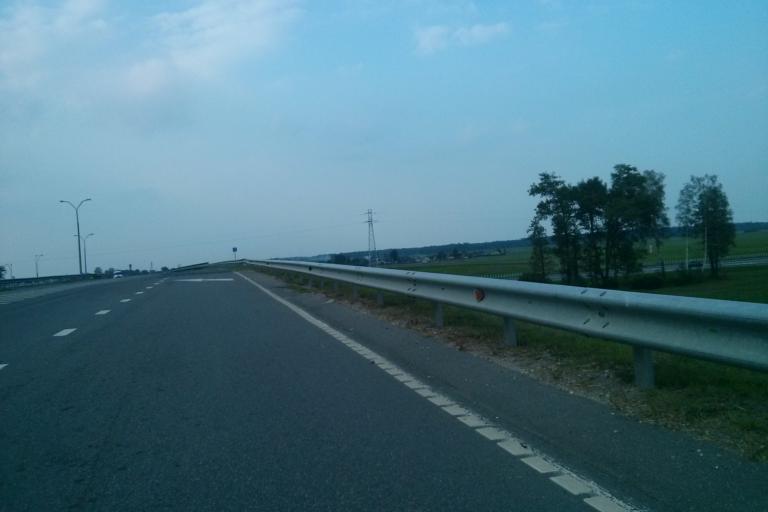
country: BY
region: Minsk
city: Chervyen'
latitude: 53.7227
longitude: 28.3949
